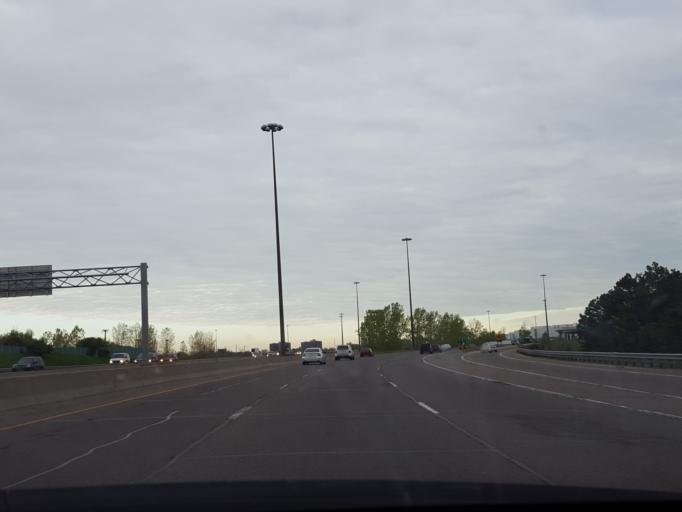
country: CA
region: Ontario
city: Etobicoke
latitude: 43.7128
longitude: -79.5128
